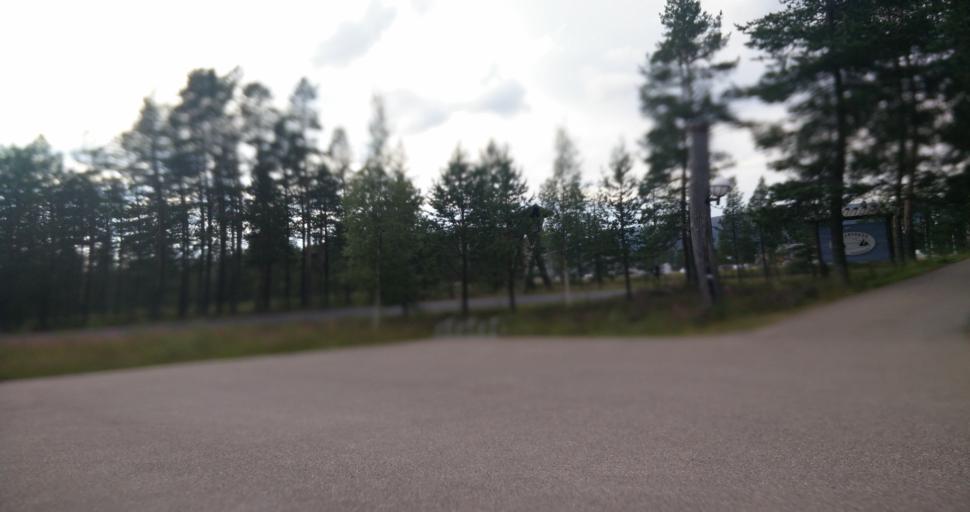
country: NO
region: Hedmark
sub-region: Trysil
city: Innbygda
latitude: 61.1780
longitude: 12.9930
